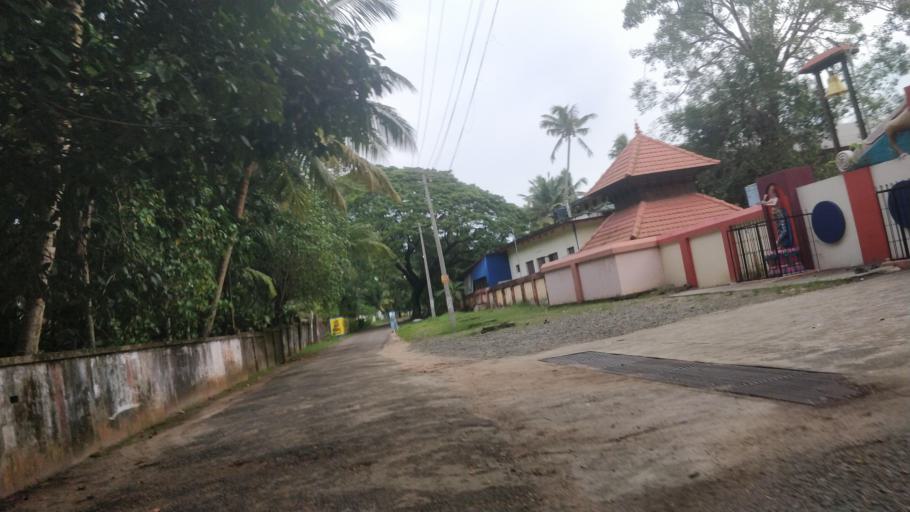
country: IN
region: Kerala
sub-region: Alappuzha
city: Shertallai
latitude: 9.6966
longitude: 76.3625
